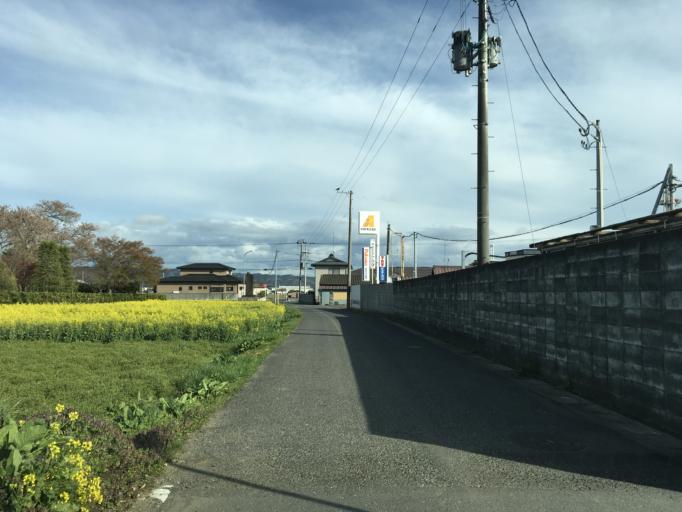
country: JP
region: Miyagi
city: Wakuya
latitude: 38.7173
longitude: 141.2466
